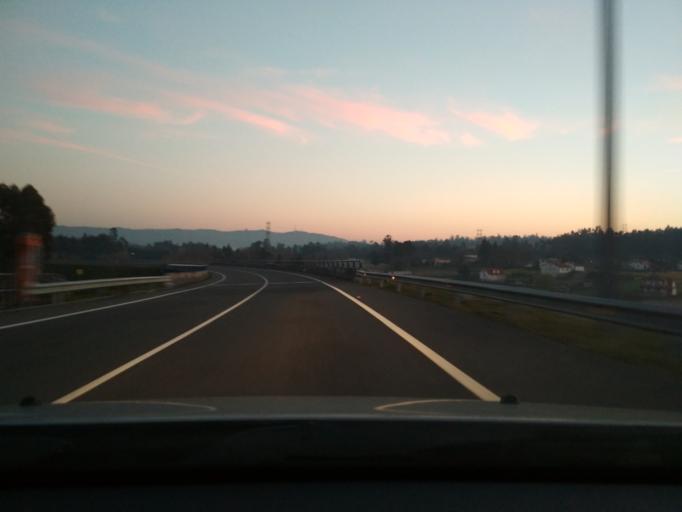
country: ES
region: Galicia
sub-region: Provincia da Coruna
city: Santiago de Compostela
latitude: 42.8448
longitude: -8.5941
